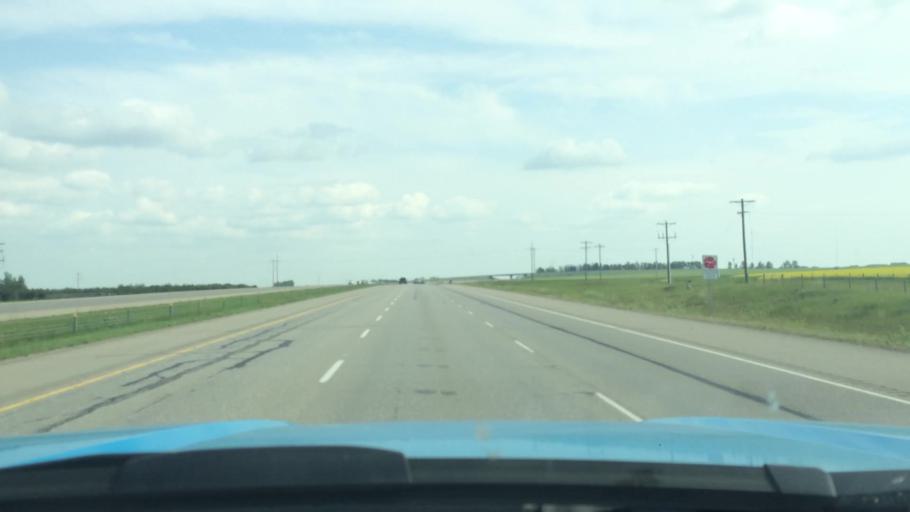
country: CA
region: Alberta
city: Crossfield
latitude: 51.4418
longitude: -114.0082
